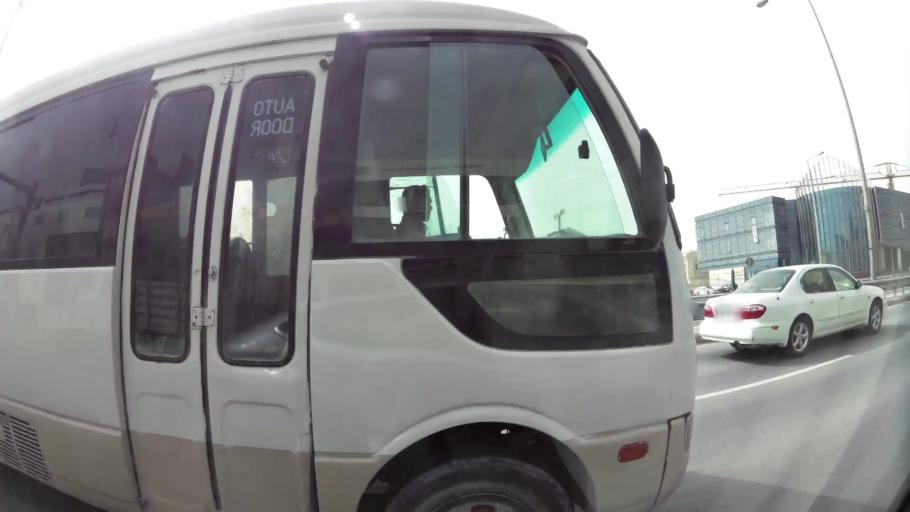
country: QA
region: Baladiyat ad Dawhah
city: Doha
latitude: 25.2640
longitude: 51.5439
